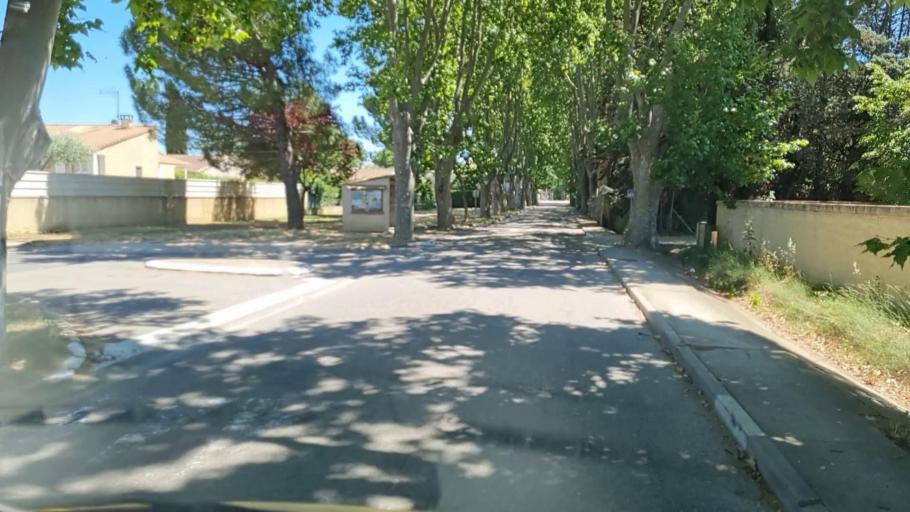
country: FR
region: Languedoc-Roussillon
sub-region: Departement du Gard
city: Le Cailar
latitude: 43.6851
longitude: 4.2330
